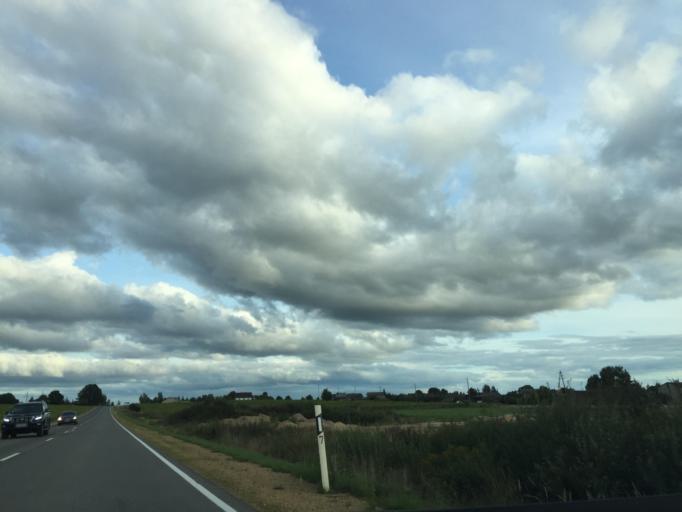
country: LV
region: Nereta
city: Nereta
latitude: 56.2151
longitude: 25.3012
